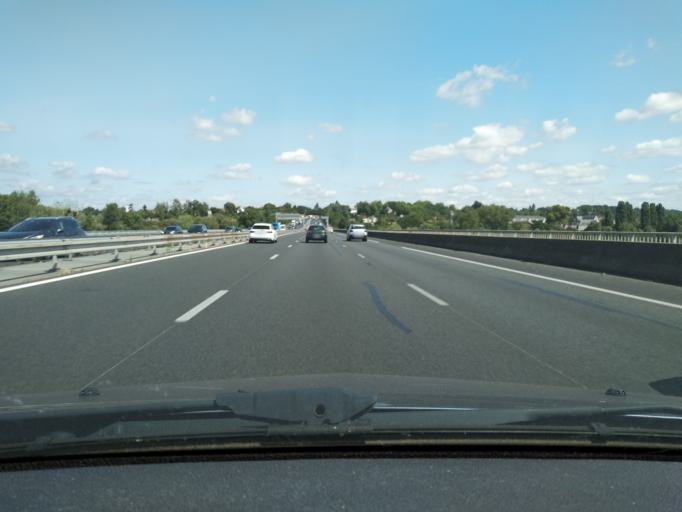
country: FR
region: Centre
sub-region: Departement d'Indre-et-Loire
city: Tours
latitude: 47.3994
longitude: 0.7101
